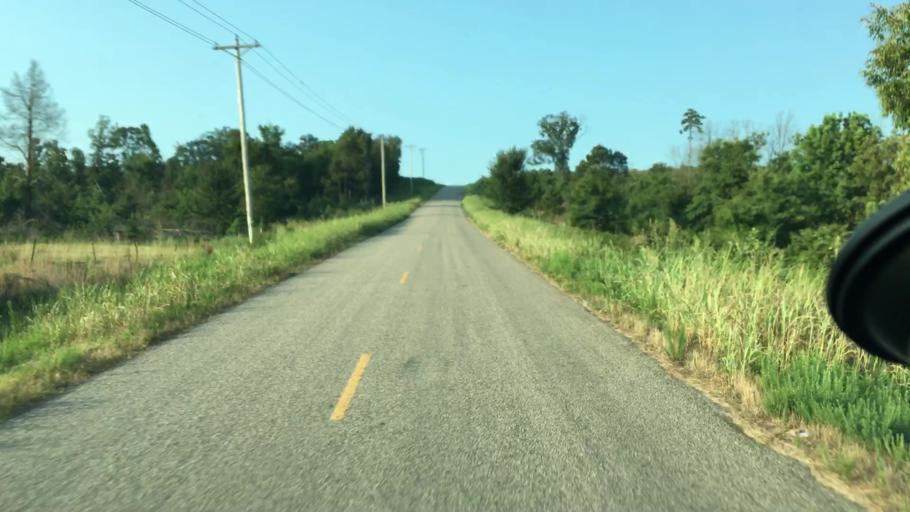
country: US
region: Arkansas
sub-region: Johnson County
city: Coal Hill
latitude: 35.3602
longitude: -93.6131
